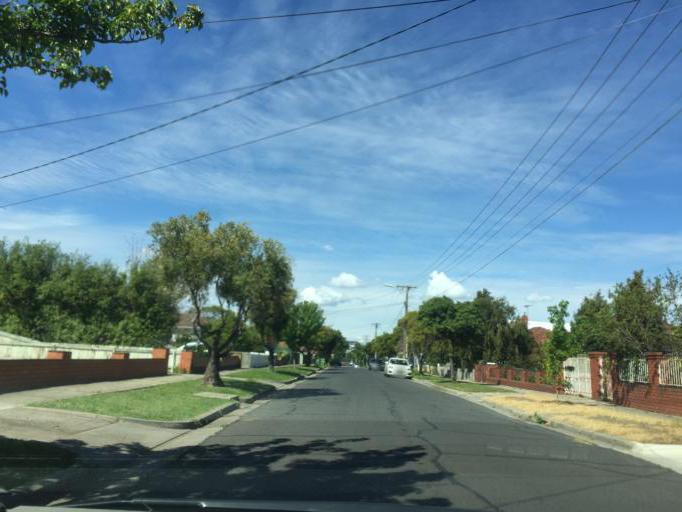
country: AU
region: Victoria
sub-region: Maribyrnong
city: Maribyrnong
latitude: -37.7823
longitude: 144.8858
